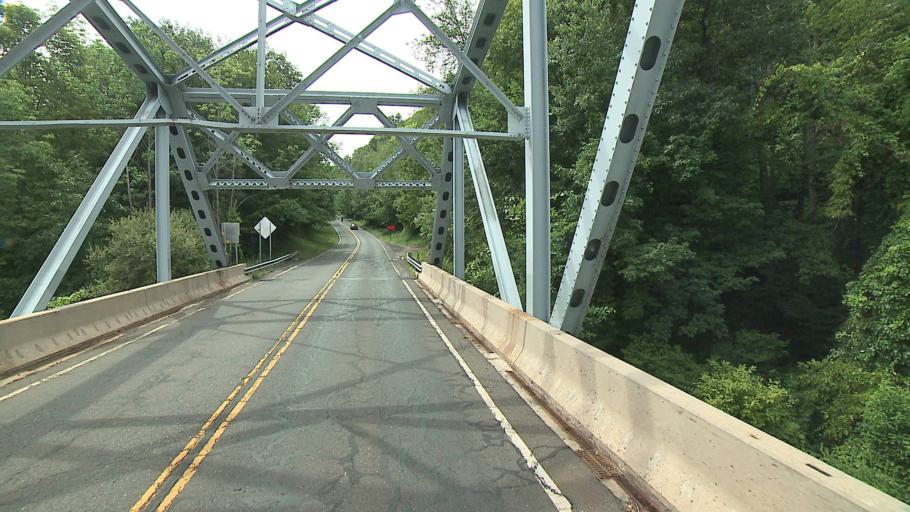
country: US
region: Connecticut
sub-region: Fairfield County
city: Newtown
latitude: 41.4786
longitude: -73.3509
